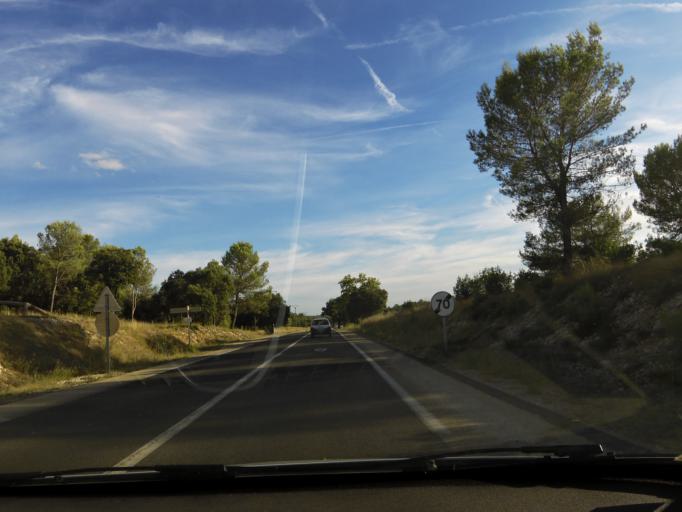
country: FR
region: Languedoc-Roussillon
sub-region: Departement de l'Herault
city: Saint-Mathieu-de-Treviers
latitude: 43.7981
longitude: 3.8766
